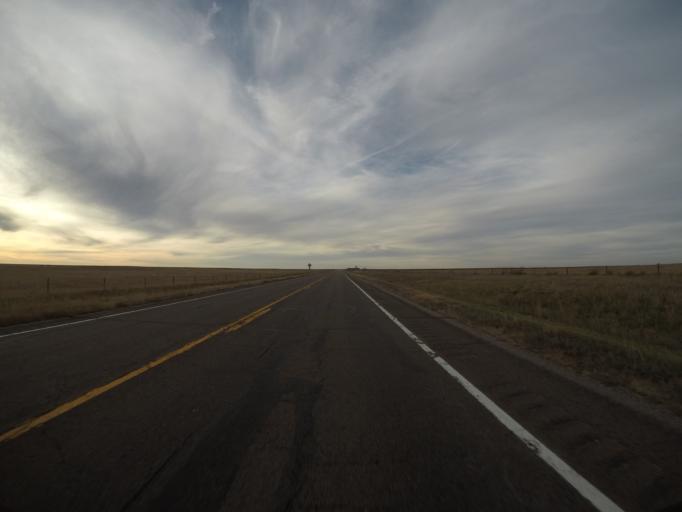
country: US
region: Colorado
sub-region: Yuma County
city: Yuma
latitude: 39.6720
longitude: -102.9545
